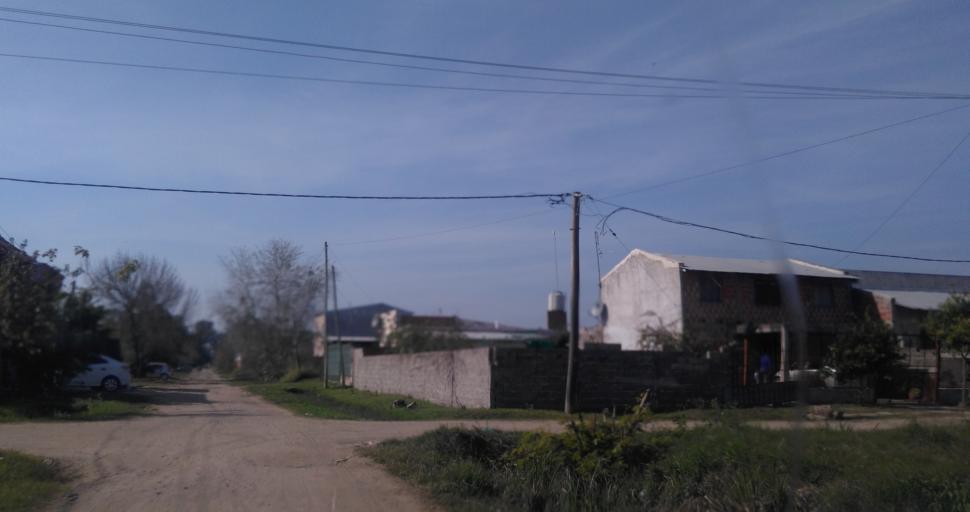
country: AR
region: Chaco
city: Fontana
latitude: -27.4450
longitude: -59.0339
